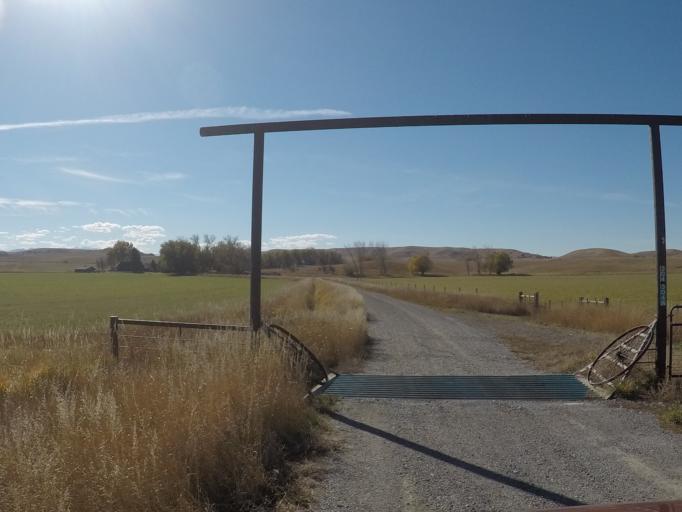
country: US
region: Montana
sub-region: Sweet Grass County
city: Big Timber
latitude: 45.8019
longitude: -109.8639
